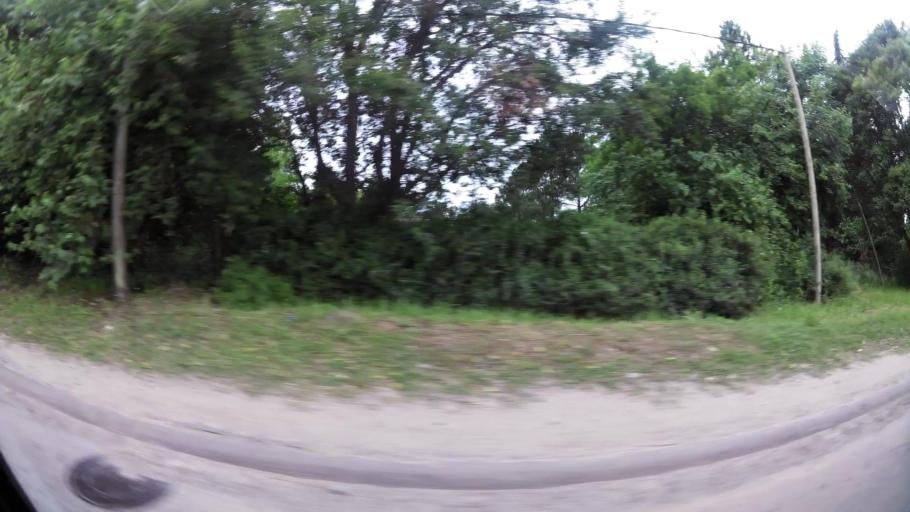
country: AR
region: Buenos Aires
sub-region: Partido de La Plata
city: La Plata
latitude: -34.9654
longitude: -58.0152
